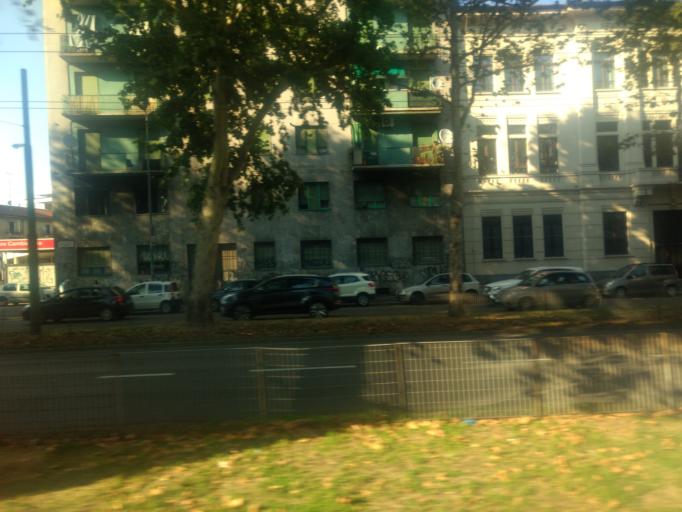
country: IT
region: Lombardy
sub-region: Citta metropolitana di Milano
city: Milano
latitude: 45.4978
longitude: 9.1676
